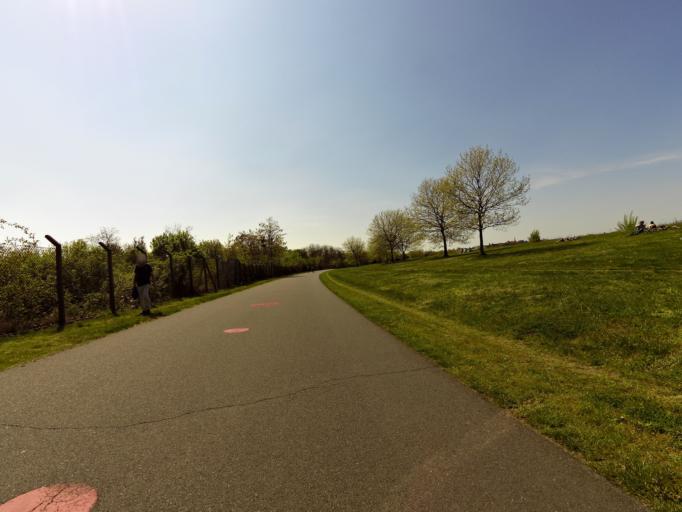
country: DE
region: Berlin
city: Tempelhof Bezirk
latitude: 52.4666
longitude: 13.4100
